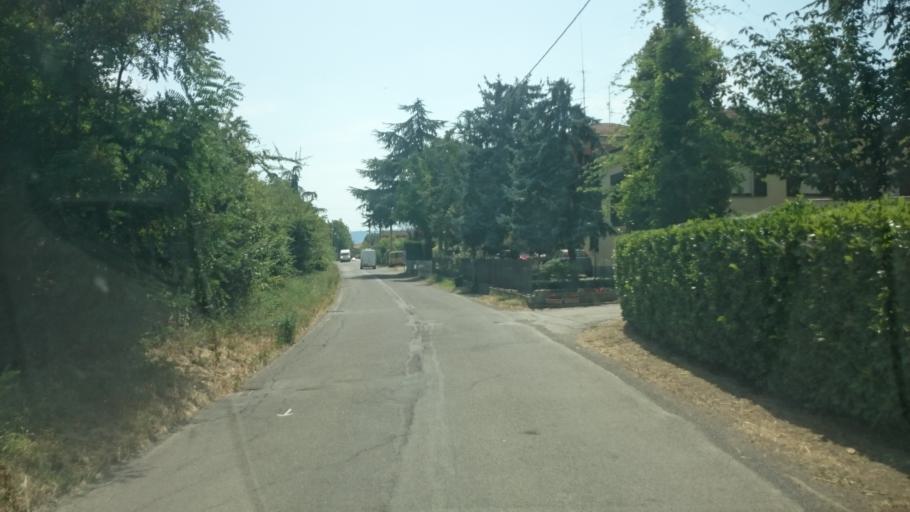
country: IT
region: Emilia-Romagna
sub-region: Provincia di Reggio Emilia
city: Fogliano
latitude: 44.6352
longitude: 10.6676
